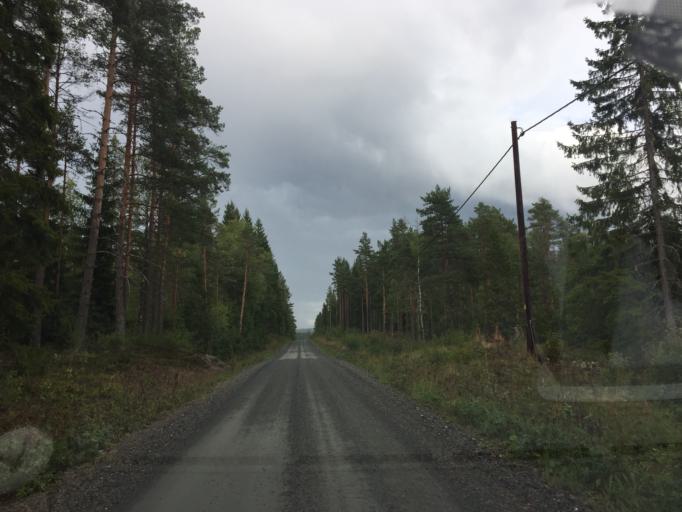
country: SE
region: Vaermland
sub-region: Filipstads Kommun
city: Lesjofors
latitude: 59.9121
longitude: 14.1097
